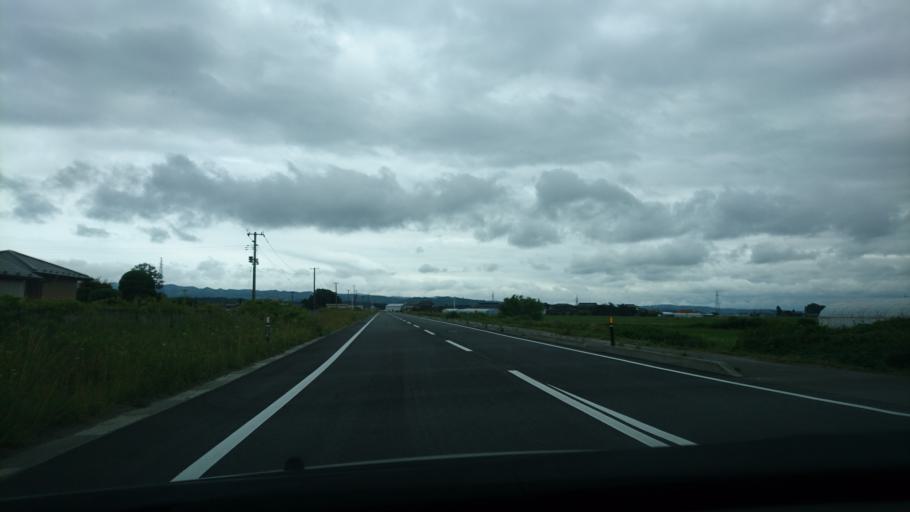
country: JP
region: Miyagi
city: Wakuya
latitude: 38.7193
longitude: 141.2561
